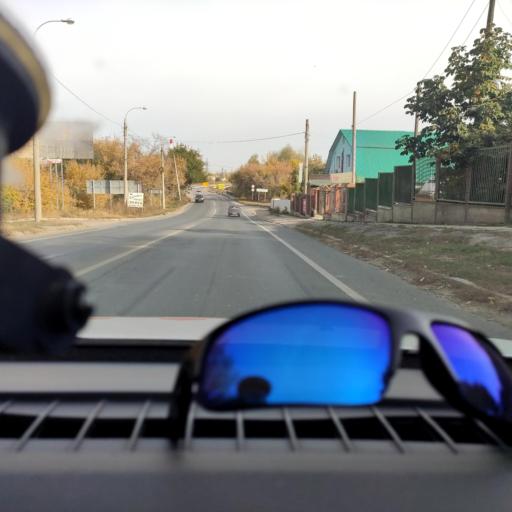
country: RU
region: Samara
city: Novokuybyshevsk
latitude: 53.0905
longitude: 50.0659
